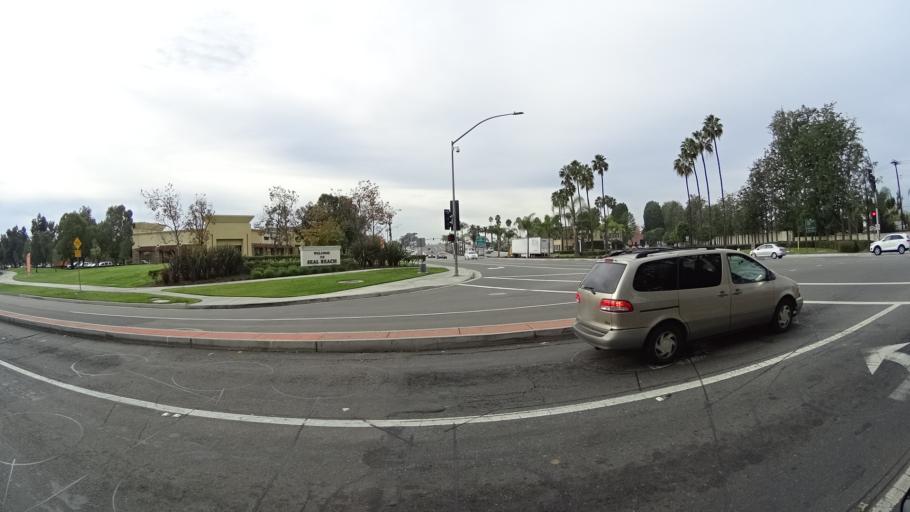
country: US
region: California
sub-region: Orange County
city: Rossmoor
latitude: 33.7779
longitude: -118.0718
